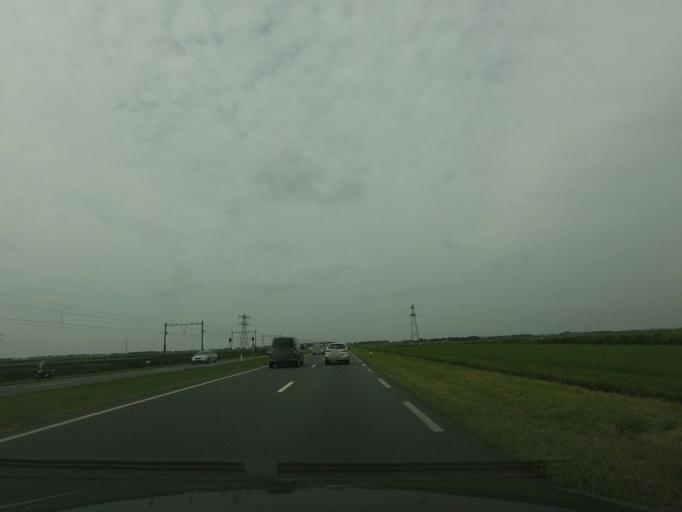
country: NL
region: North Holland
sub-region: Gemeente Uitgeest
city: Uitgeest
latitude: 52.5034
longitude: 4.7377
